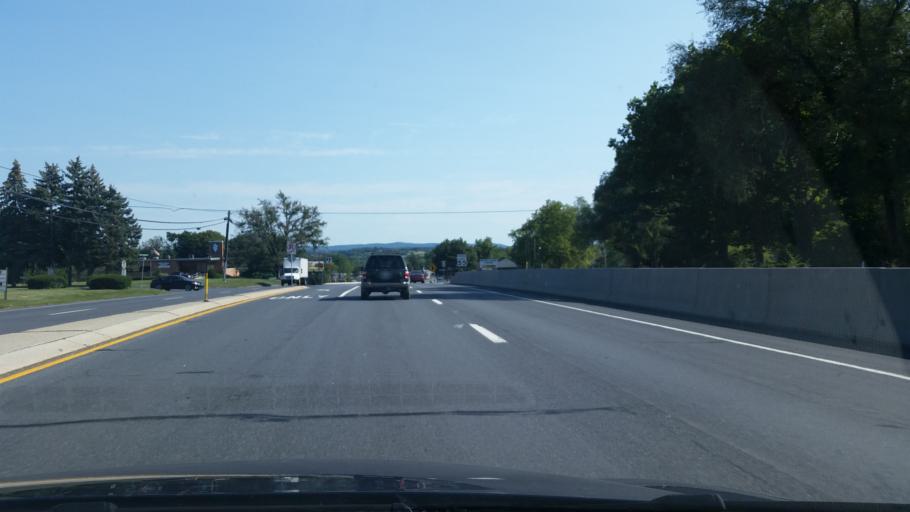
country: US
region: Pennsylvania
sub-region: Berks County
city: Shoemakersville
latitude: 40.5233
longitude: -75.9721
